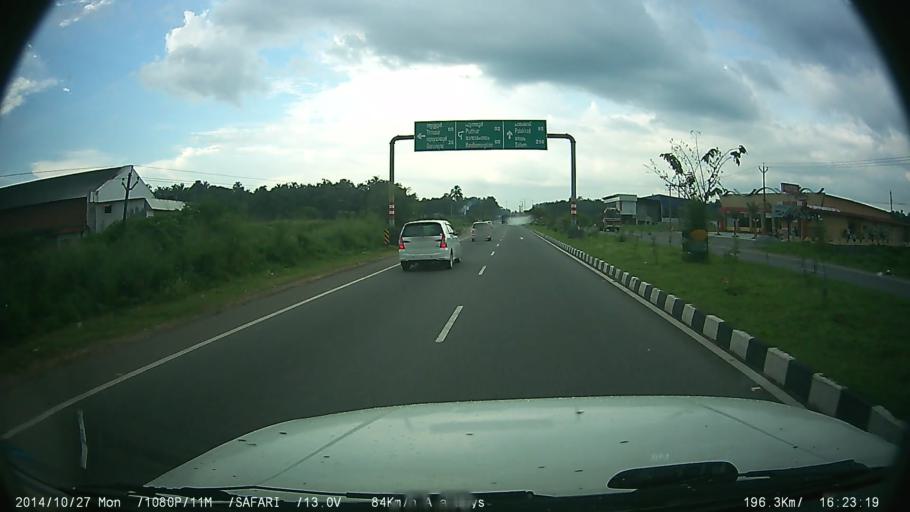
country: IN
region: Kerala
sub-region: Thrissur District
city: Trichur
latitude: 10.4842
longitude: 76.2578
